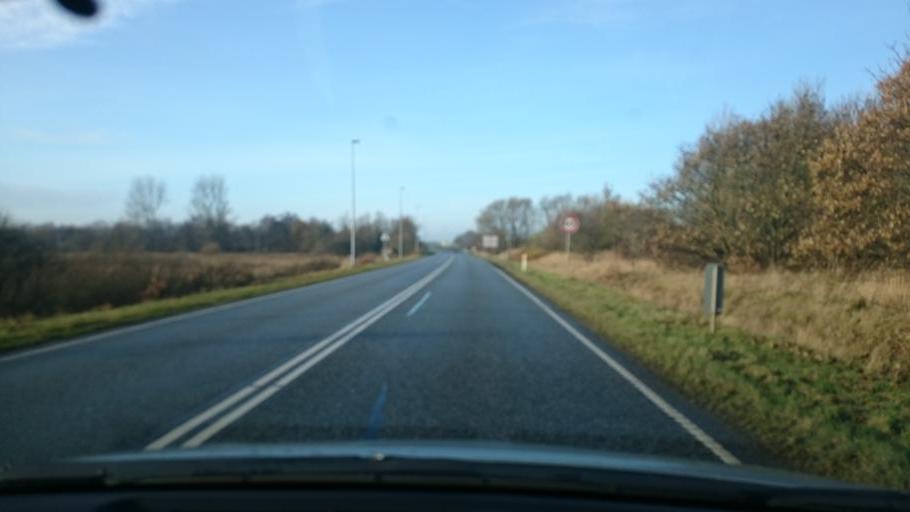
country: DK
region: South Denmark
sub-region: Esbjerg Kommune
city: Ribe
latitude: 55.3198
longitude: 8.7648
